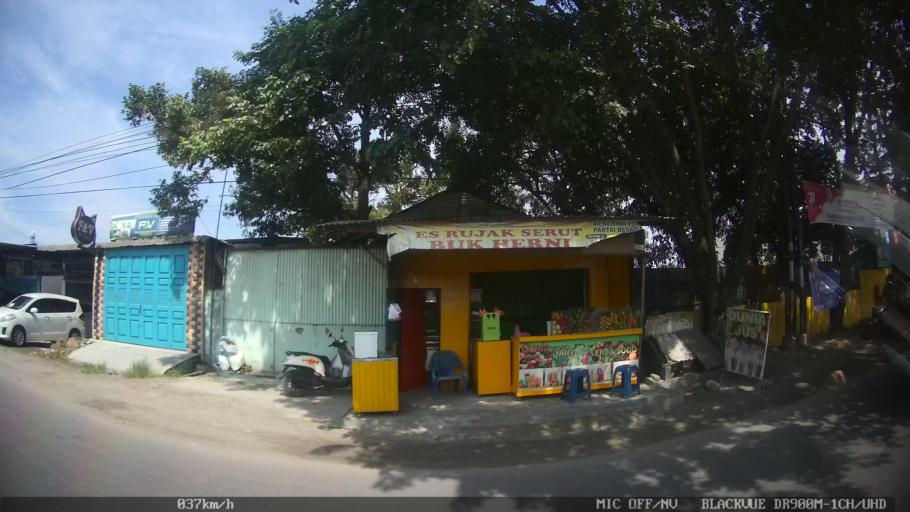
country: ID
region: North Sumatra
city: Medan
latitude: 3.6434
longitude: 98.6577
